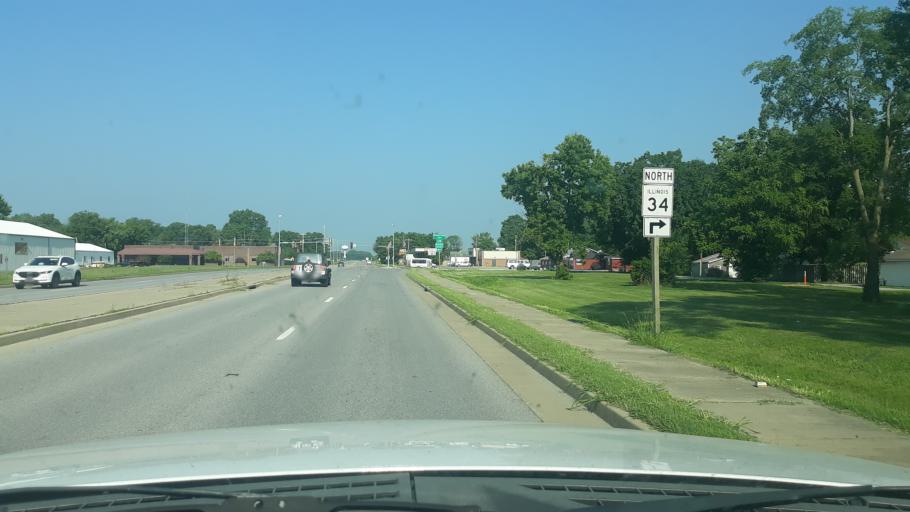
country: US
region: Illinois
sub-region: Saline County
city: Harrisburg
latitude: 37.7434
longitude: -88.5378
